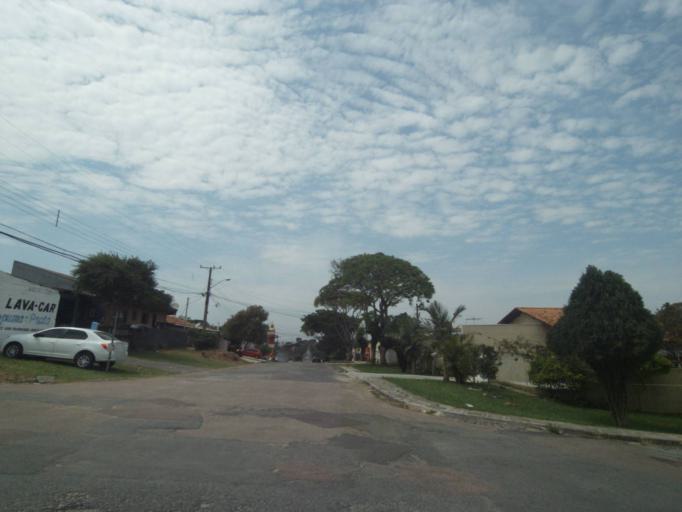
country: BR
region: Parana
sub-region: Pinhais
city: Pinhais
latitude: -25.4024
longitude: -49.2085
